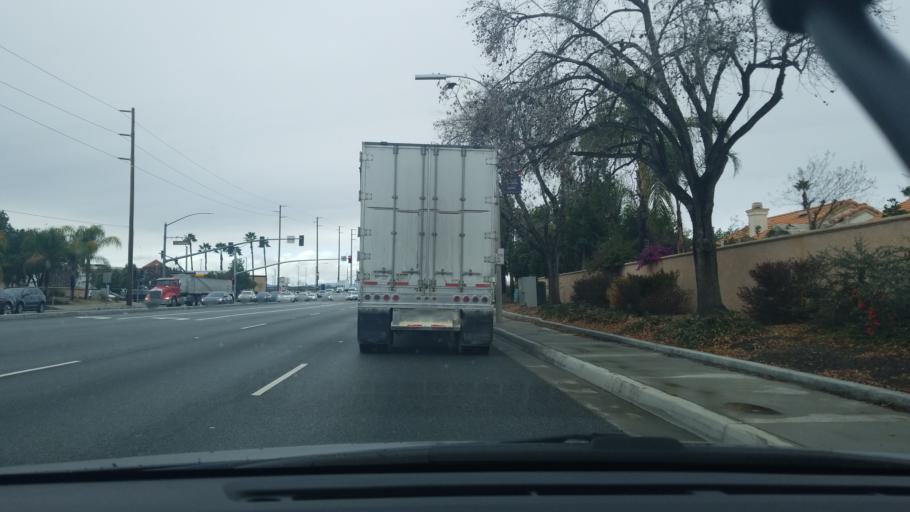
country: US
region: California
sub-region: Riverside County
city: Sun City
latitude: 33.6852
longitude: -117.1661
